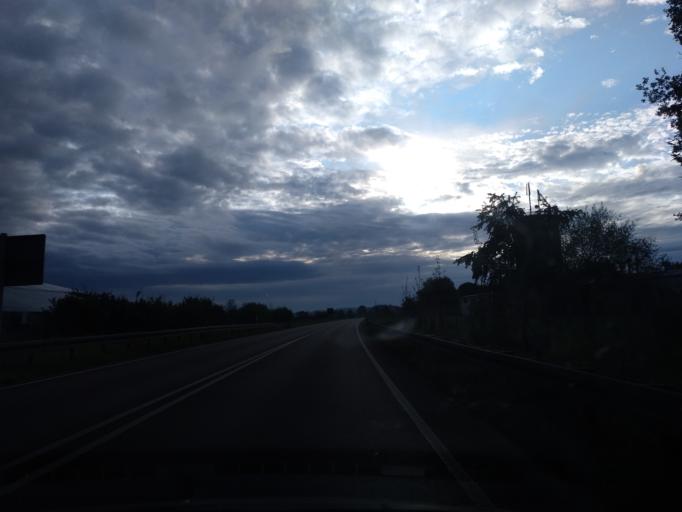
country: DE
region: Bavaria
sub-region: Upper Bavaria
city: Burgheim
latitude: 48.7099
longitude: 11.0085
